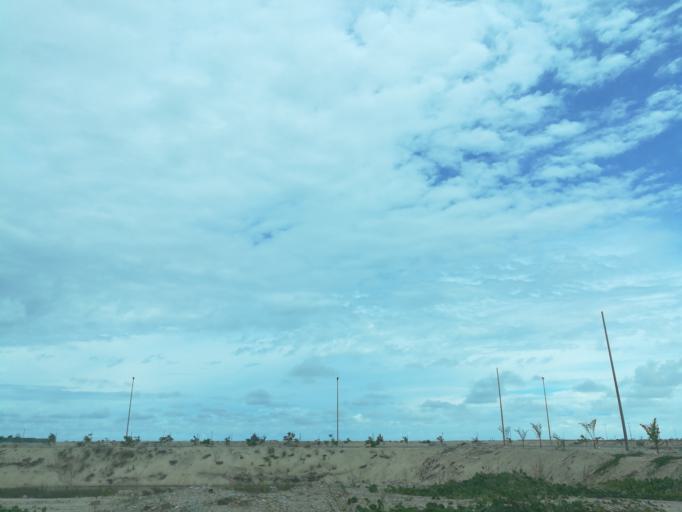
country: NG
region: Lagos
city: Ikoyi
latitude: 6.4116
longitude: 3.4210
